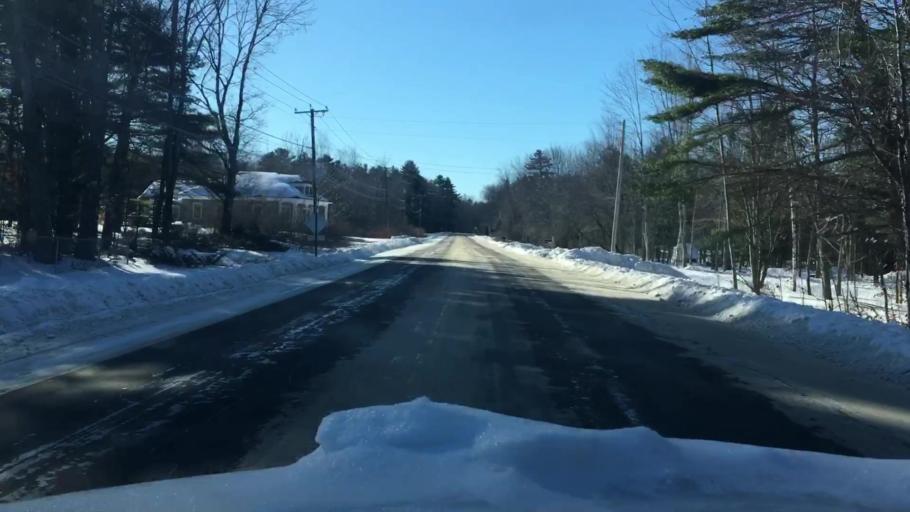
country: US
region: Maine
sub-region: Cumberland County
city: Brunswick
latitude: 43.9455
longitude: -69.9287
